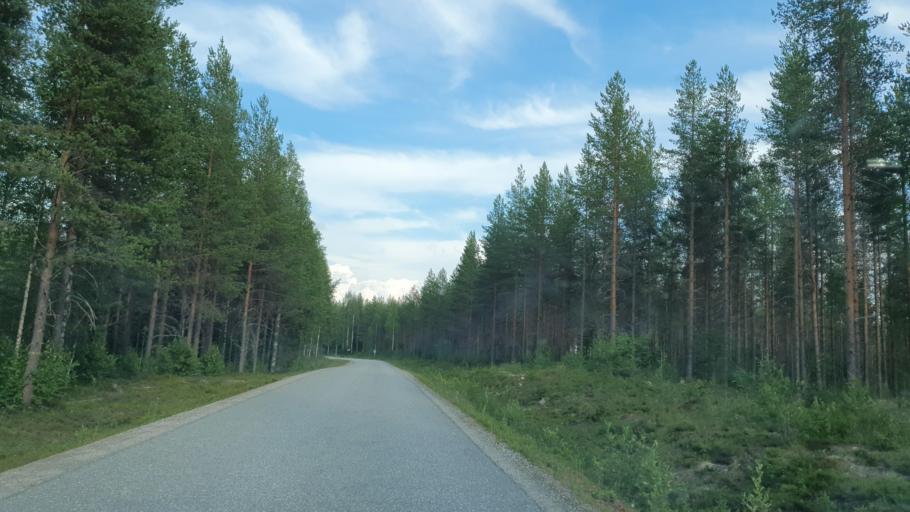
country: FI
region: Kainuu
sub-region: Kehys-Kainuu
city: Kuhmo
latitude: 64.2765
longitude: 29.4359
